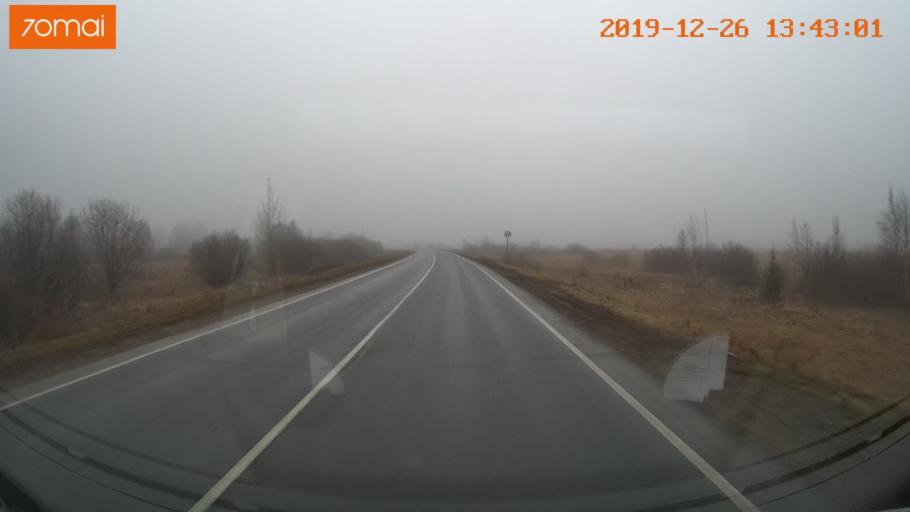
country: RU
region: Vologda
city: Sheksna
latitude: 58.7133
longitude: 38.4799
